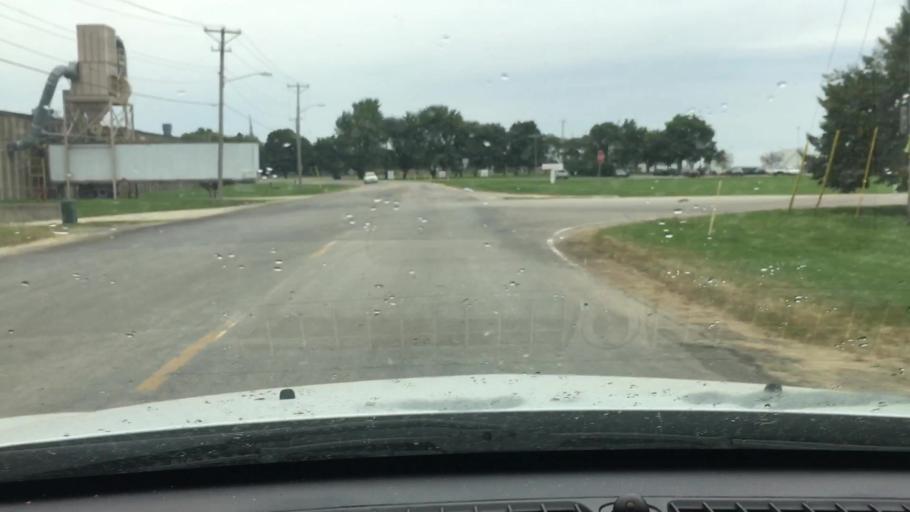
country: US
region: Illinois
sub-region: Ogle County
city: Rochelle
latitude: 41.9073
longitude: -89.0540
